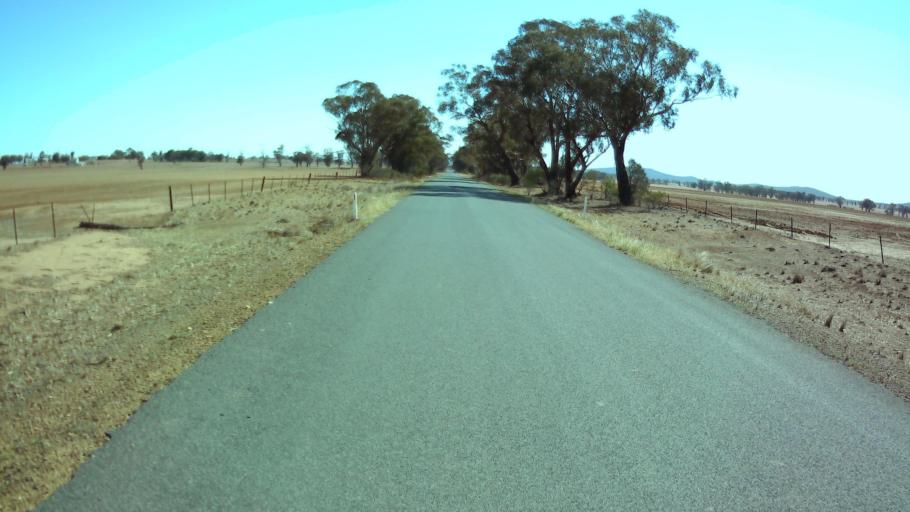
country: AU
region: New South Wales
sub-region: Weddin
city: Grenfell
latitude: -33.7469
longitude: 147.8772
